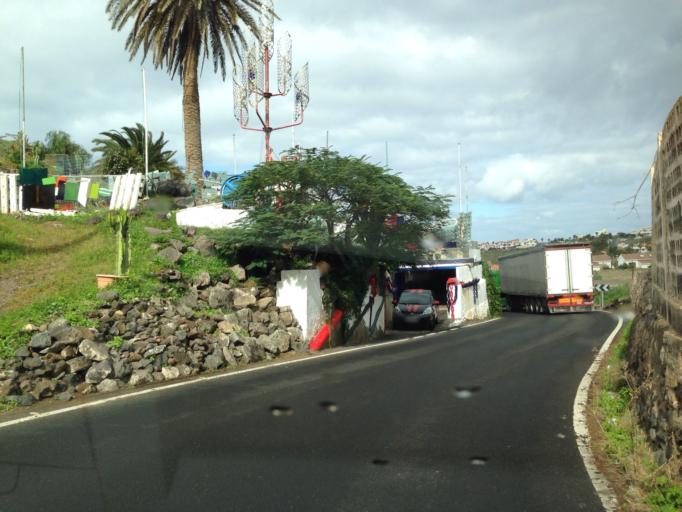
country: ES
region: Canary Islands
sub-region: Provincia de Las Palmas
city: Agaete
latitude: 28.0980
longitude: -15.7037
